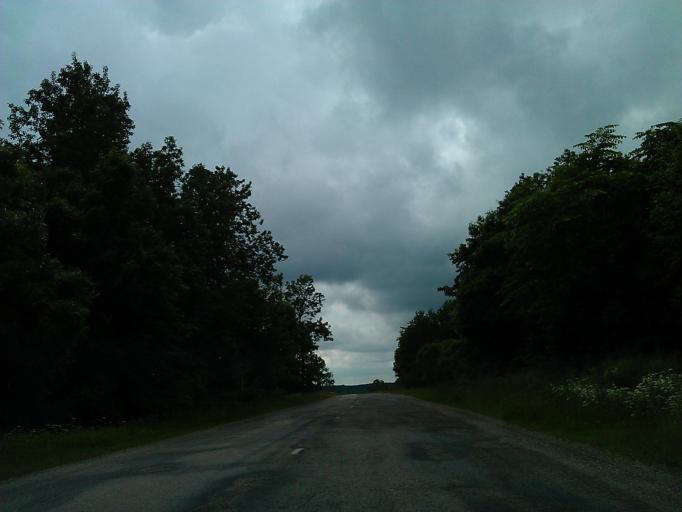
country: LV
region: Aizpute
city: Aizpute
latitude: 56.8318
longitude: 21.7501
